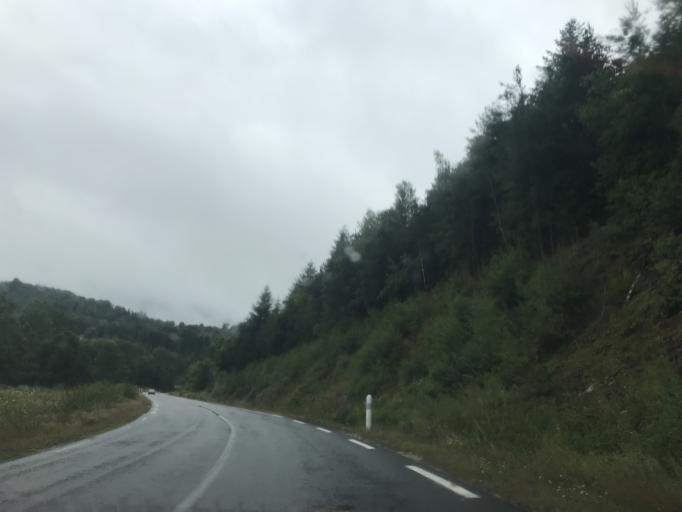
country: FR
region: Auvergne
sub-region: Departement du Puy-de-Dome
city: Job
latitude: 45.6379
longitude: 3.7127
